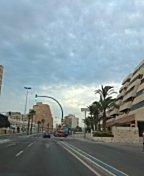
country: ES
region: Murcia
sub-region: Murcia
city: La Manga del Mar Menor
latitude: 37.6921
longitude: -0.7378
